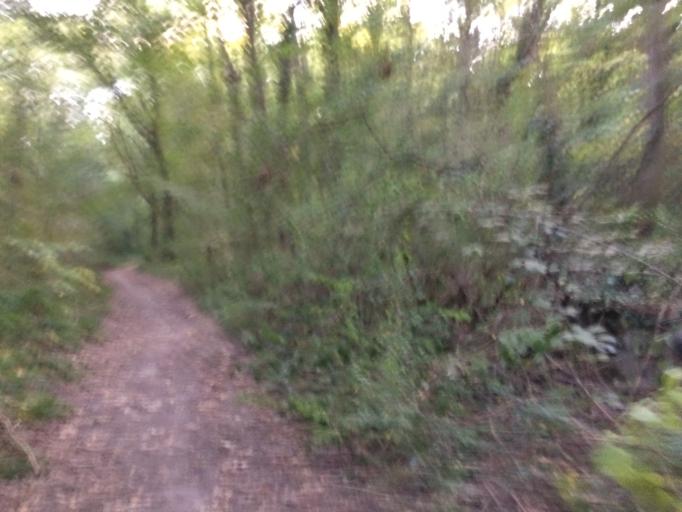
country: FR
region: Ile-de-France
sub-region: Departement de l'Essonne
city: Nozay
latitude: 48.6607
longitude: 2.2127
